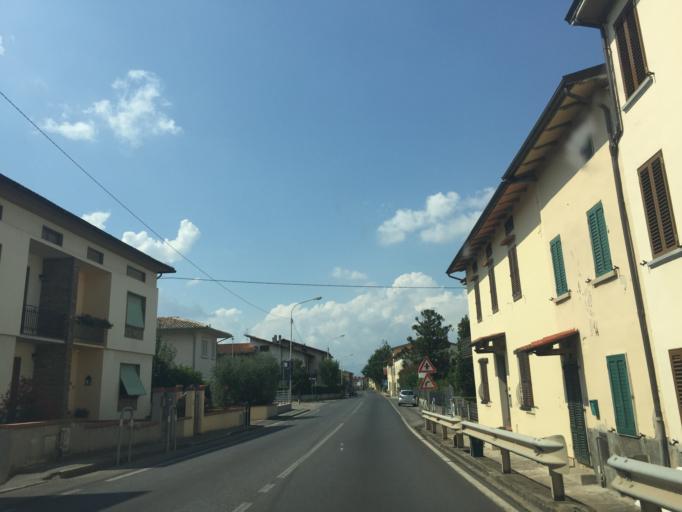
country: IT
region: Tuscany
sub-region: Provincia di Pistoia
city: Catena
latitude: 43.8403
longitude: 11.0202
